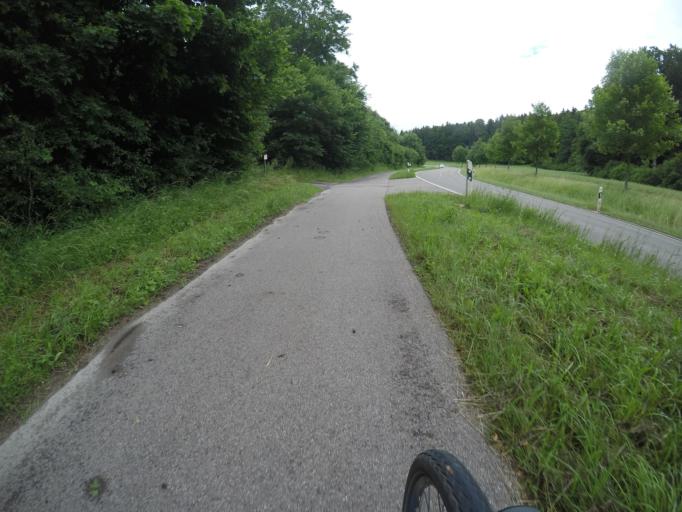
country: DE
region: Baden-Wuerttemberg
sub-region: Regierungsbezirk Stuttgart
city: Gartringen
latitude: 48.6575
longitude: 8.8815
